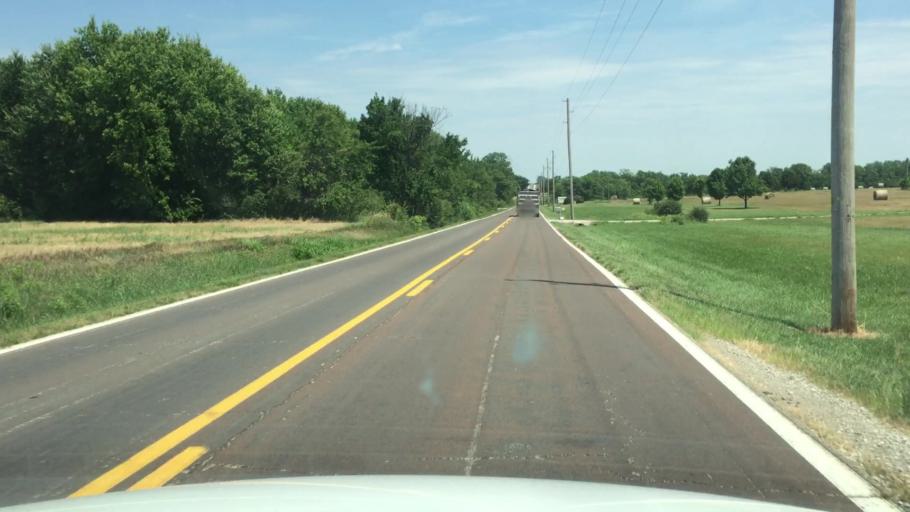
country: US
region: Kansas
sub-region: Shawnee County
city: Topeka
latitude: 38.9860
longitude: -95.5323
